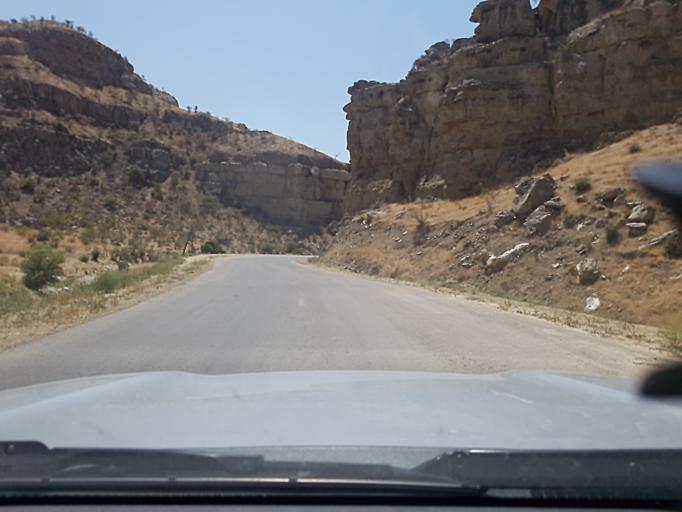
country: TM
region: Balkan
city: Magtymguly
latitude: 38.4201
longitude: 56.6409
